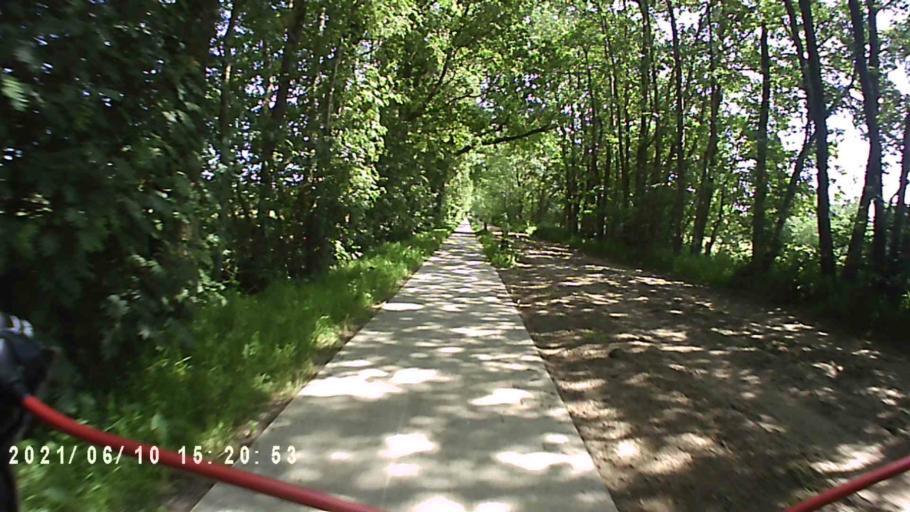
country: NL
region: Friesland
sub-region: Gemeente Achtkarspelen
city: Surhuisterveen
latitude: 53.1913
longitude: 6.1788
